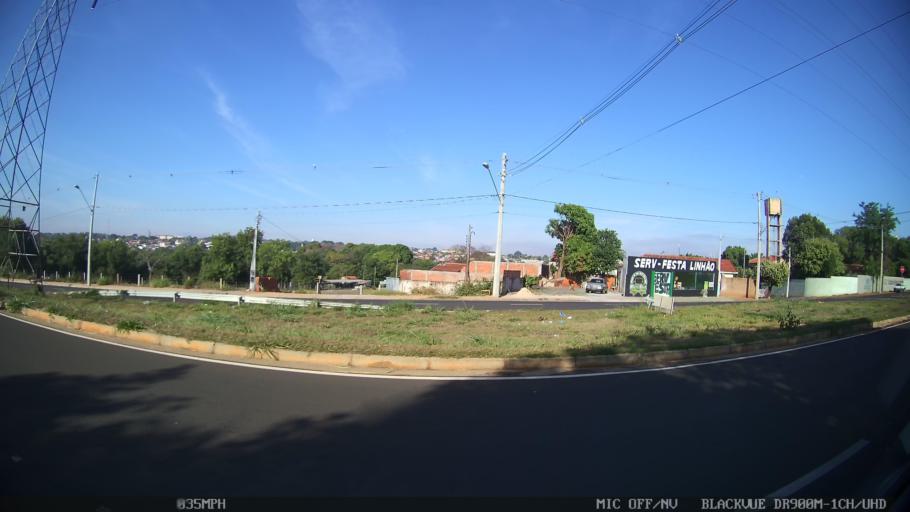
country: BR
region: Sao Paulo
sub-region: Sao Jose Do Rio Preto
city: Sao Jose do Rio Preto
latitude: -20.7638
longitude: -49.3625
